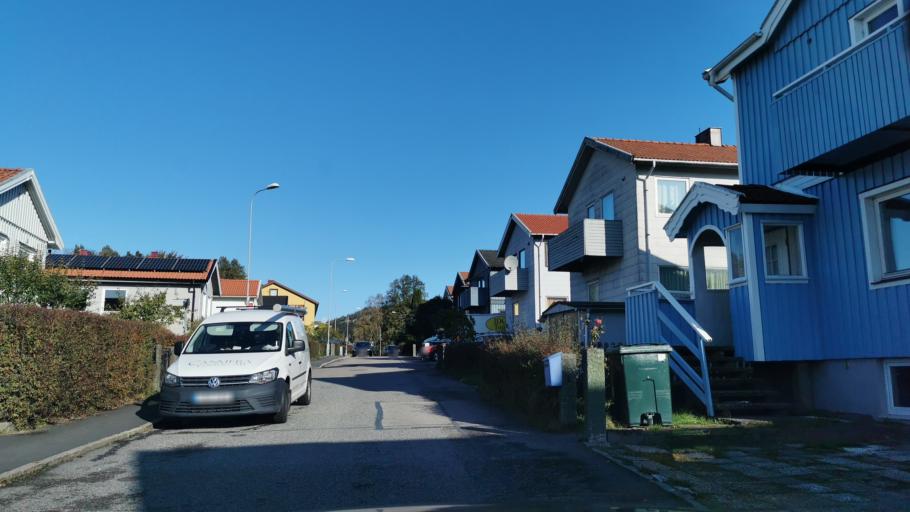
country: SE
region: Vaestra Goetaland
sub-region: Goteborg
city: Eriksbo
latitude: 57.7360
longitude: 12.0599
